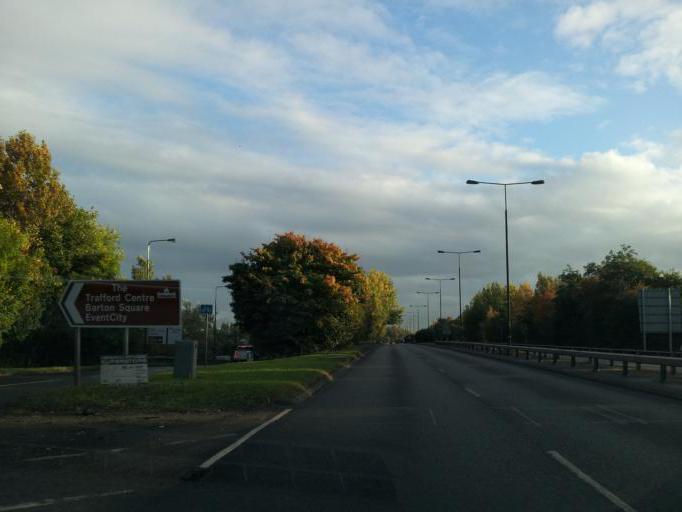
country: GB
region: England
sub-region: Trafford
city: Urmston
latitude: 53.4610
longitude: -2.3359
